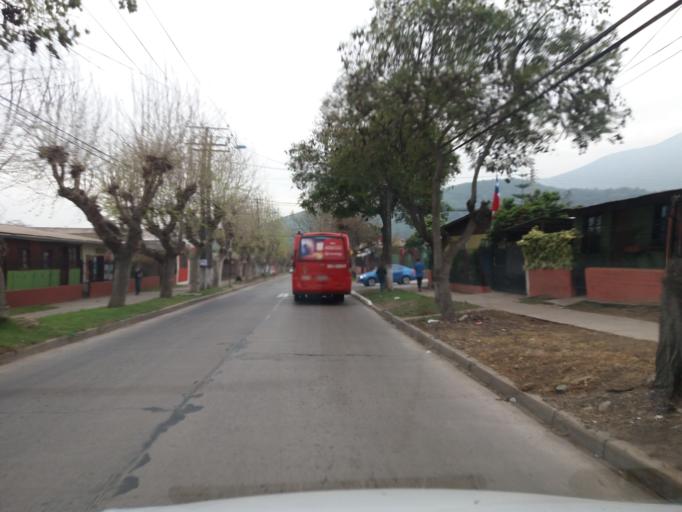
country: CL
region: Valparaiso
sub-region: Provincia de Quillota
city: Hacienda La Calera
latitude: -32.7971
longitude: -71.1470
